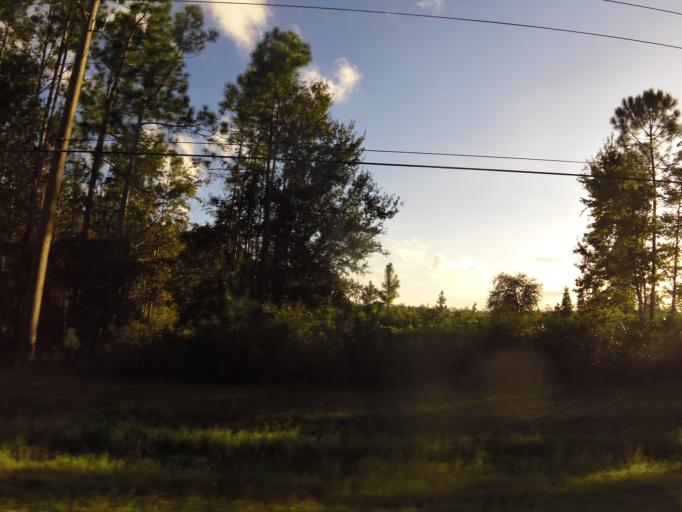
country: US
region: Florida
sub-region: Saint Johns County
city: Fruit Cove
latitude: 30.0569
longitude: -81.6222
